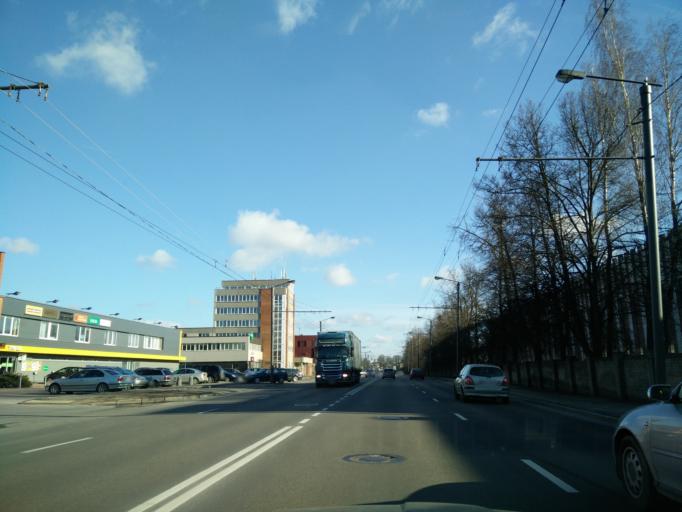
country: LT
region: Kauno apskritis
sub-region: Kauno rajonas
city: Akademija (Kaunas)
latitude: 54.9144
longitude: 23.8398
